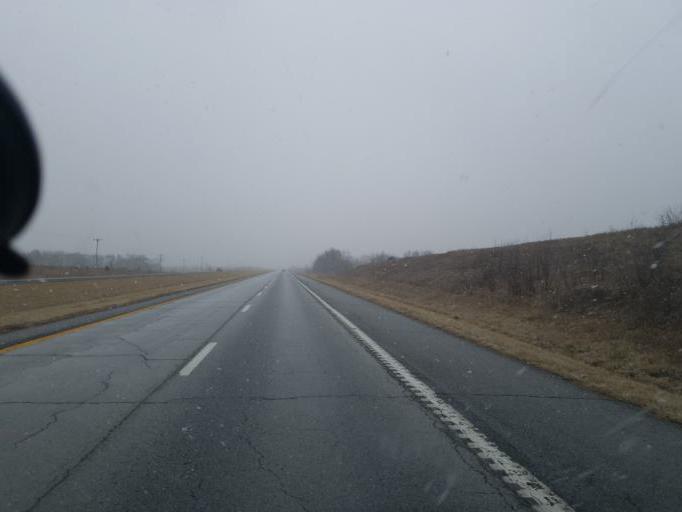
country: US
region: Missouri
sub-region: Macon County
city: La Plata
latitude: 39.9673
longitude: -92.4765
